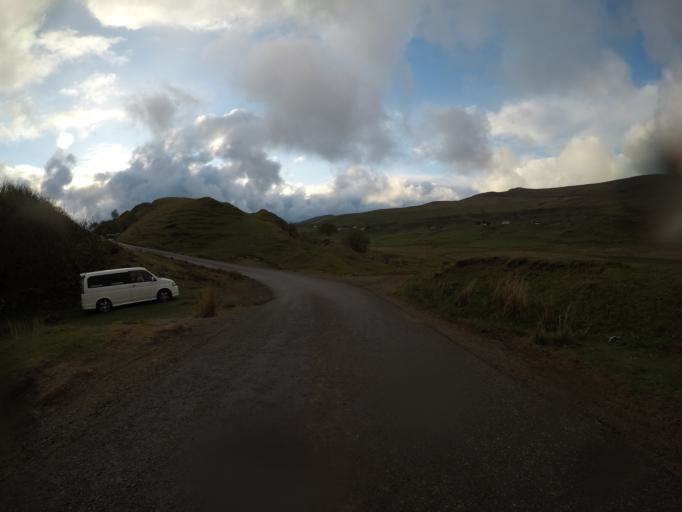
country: GB
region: Scotland
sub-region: Highland
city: Portree
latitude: 57.5836
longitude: -6.3233
